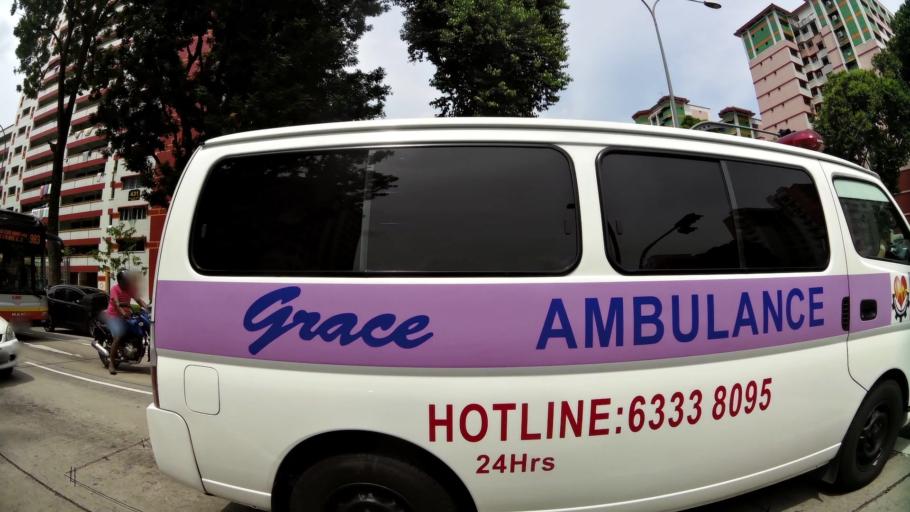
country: MY
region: Johor
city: Johor Bahru
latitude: 1.3839
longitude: 103.7424
